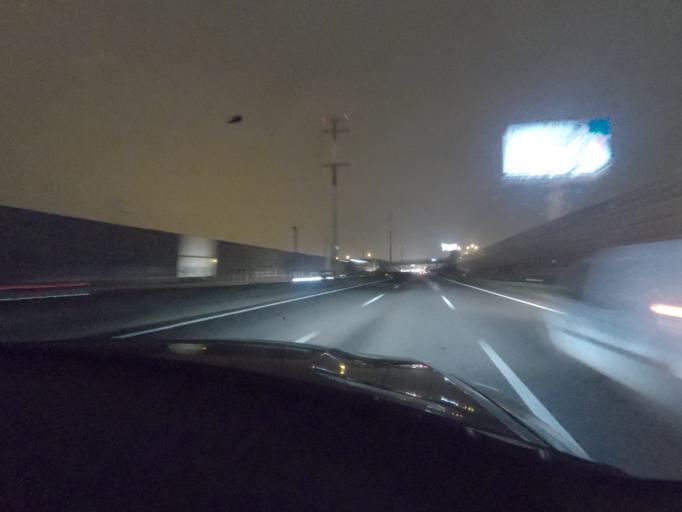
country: PT
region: Lisbon
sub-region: Loures
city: Santa Iria da Azoia
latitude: 38.8366
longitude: -9.0958
